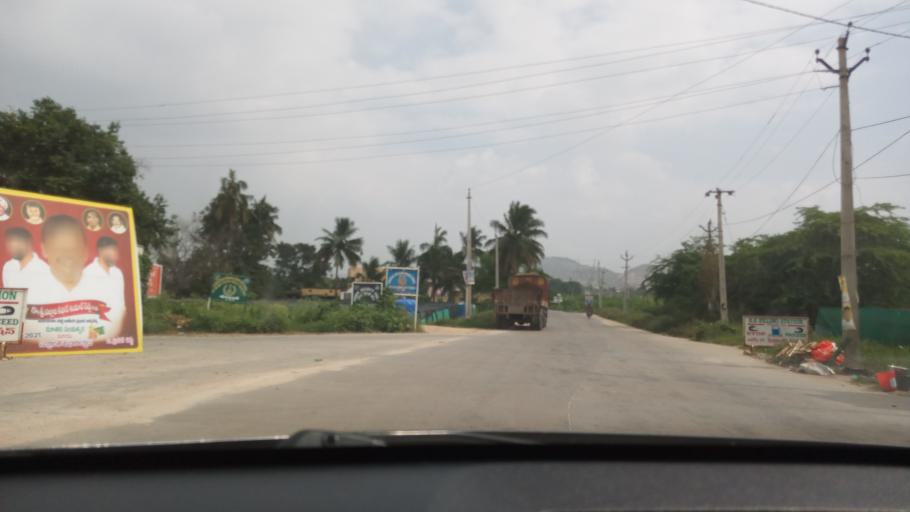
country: IN
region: Andhra Pradesh
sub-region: Chittoor
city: Madanapalle
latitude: 13.6525
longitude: 78.8081
